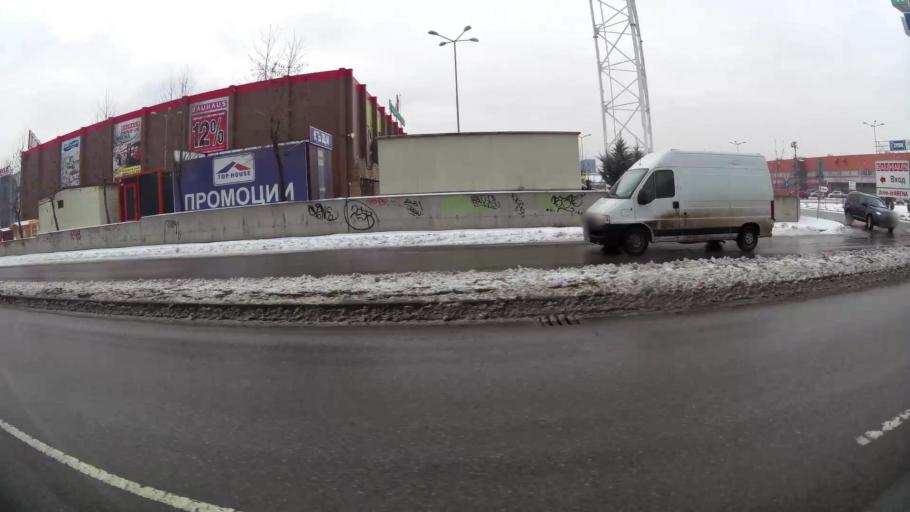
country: BG
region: Sofia-Capital
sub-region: Stolichna Obshtina
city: Sofia
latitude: 42.7182
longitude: 23.3168
